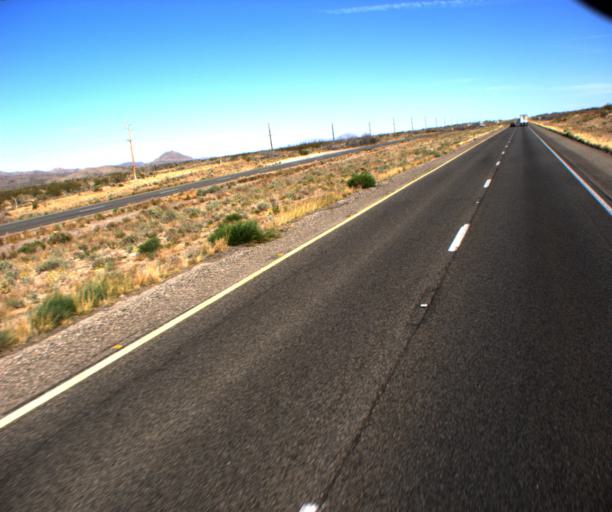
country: US
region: Arizona
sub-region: Mohave County
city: Golden Valley
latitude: 35.3506
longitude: -114.2256
